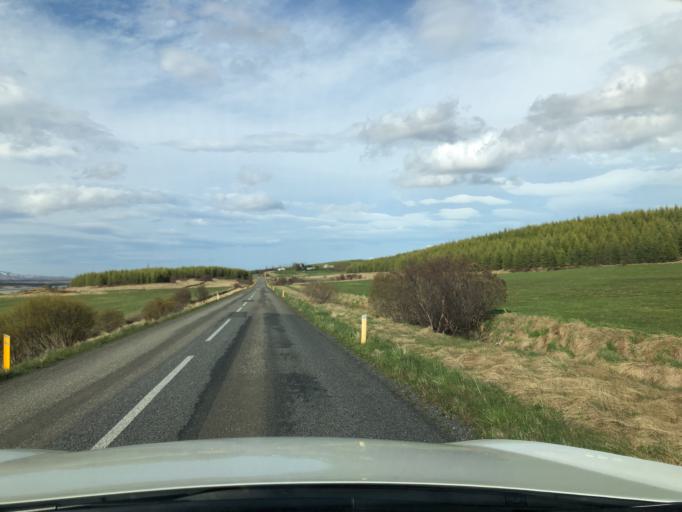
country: IS
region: East
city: Egilsstadir
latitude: 65.1624
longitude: -14.6050
